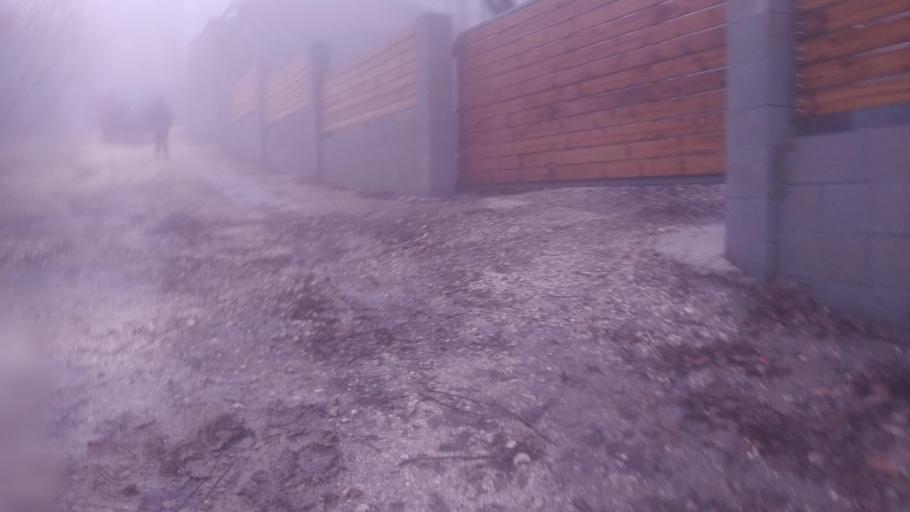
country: HU
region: Pest
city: Pilisszentkereszt
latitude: 47.7174
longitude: 18.8922
